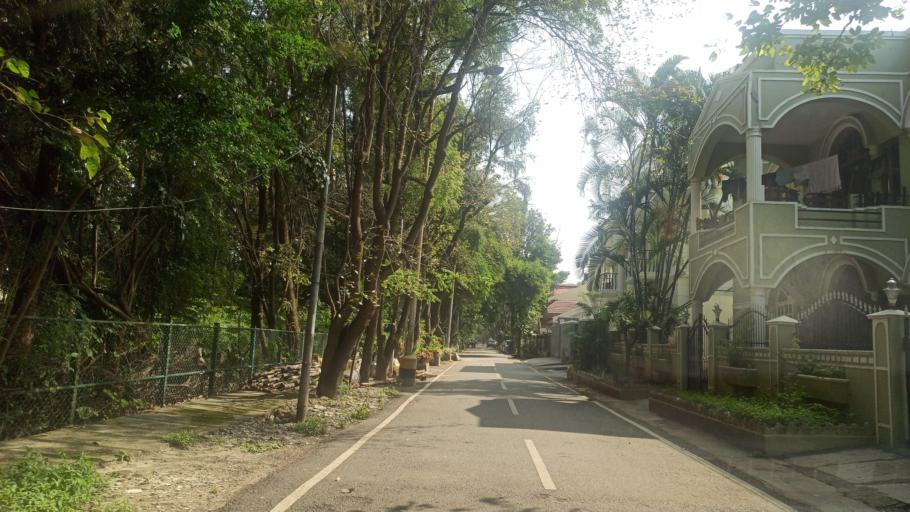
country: IN
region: Karnataka
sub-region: Bangalore Urban
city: Bangalore
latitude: 12.9165
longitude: 77.6265
